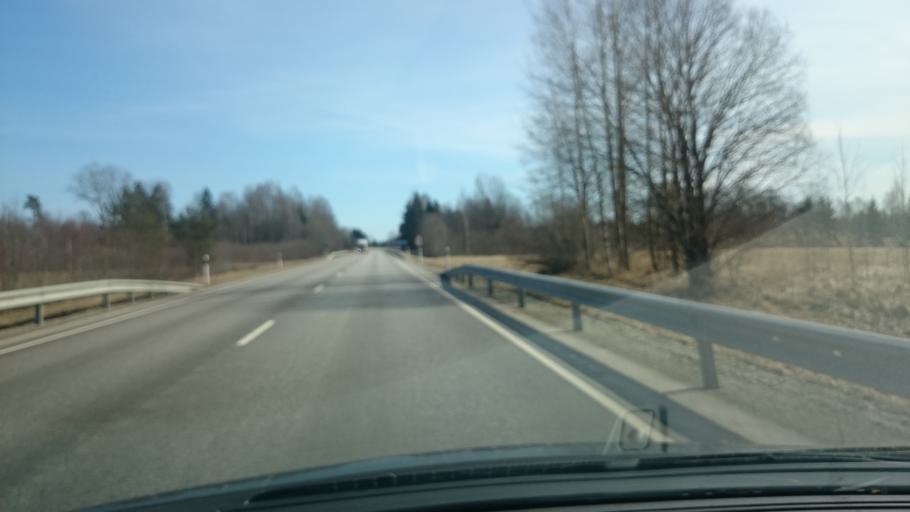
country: EE
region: Paernumaa
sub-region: Vaendra vald (alev)
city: Vandra
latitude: 58.6686
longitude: 25.1400
